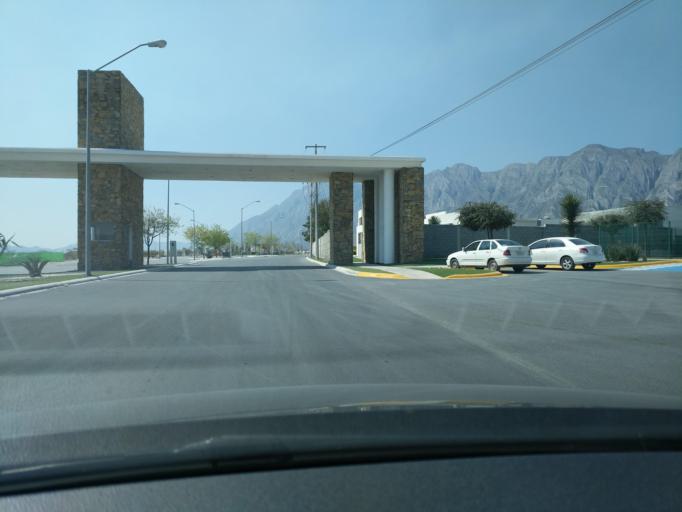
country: MX
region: Nuevo Leon
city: Garcia
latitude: 25.8141
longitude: -100.5376
